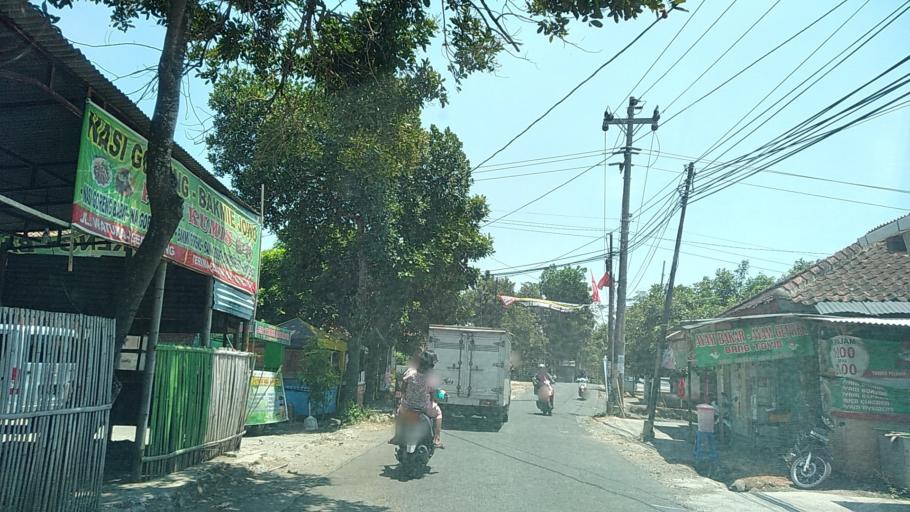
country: ID
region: Central Java
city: Ungaran
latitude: -7.0875
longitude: 110.4238
